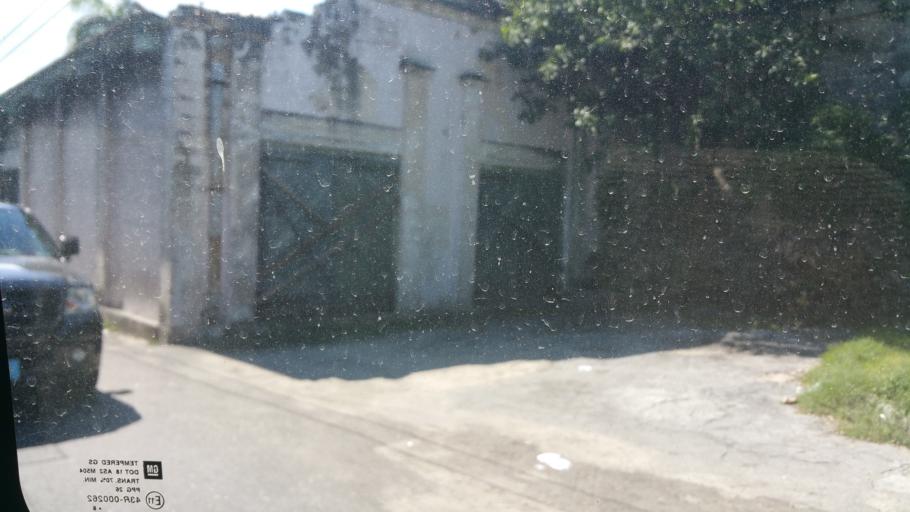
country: BS
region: New Providence
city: Nassau
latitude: 25.0726
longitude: -77.3401
